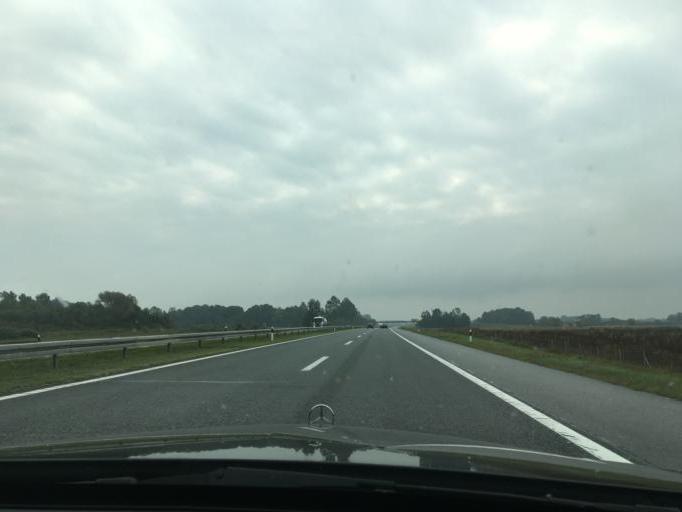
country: HR
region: Brodsko-Posavska
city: Resetari
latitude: 45.2247
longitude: 17.4845
